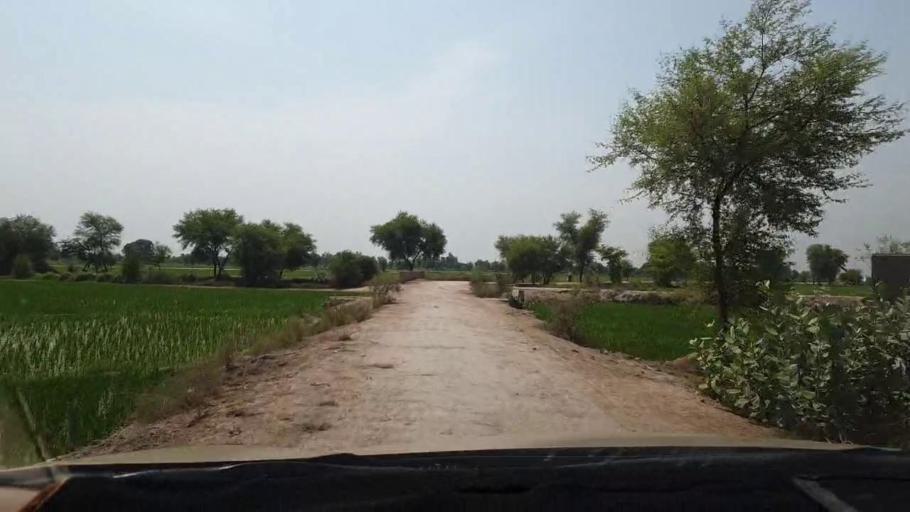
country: PK
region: Sindh
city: Naudero
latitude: 27.6453
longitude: 68.2747
